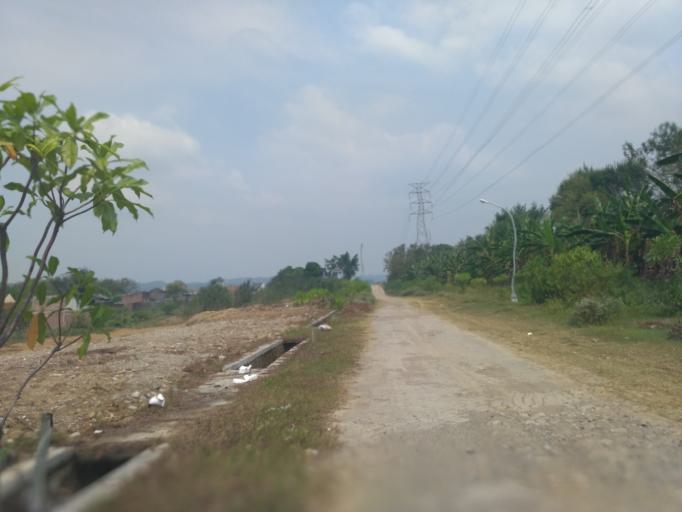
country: ID
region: Central Java
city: Mranggen
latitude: -7.0643
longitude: 110.4618
